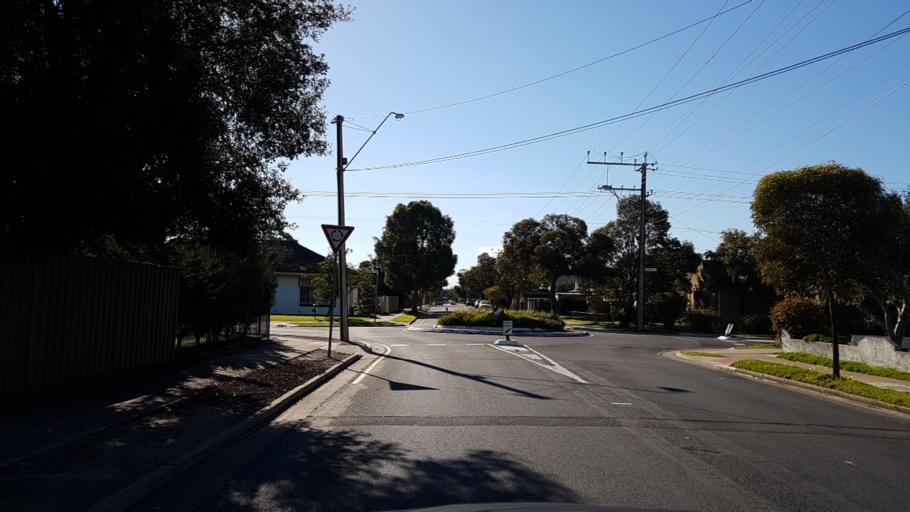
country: AU
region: South Australia
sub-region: City of West Torrens
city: Plympton
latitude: -34.9642
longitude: 138.5453
